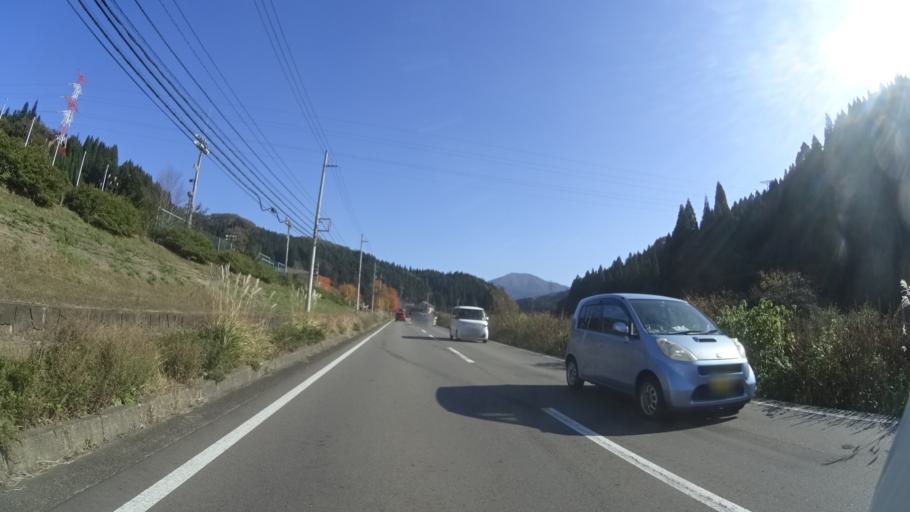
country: JP
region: Fukui
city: Ono
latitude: 36.0053
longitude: 136.4005
